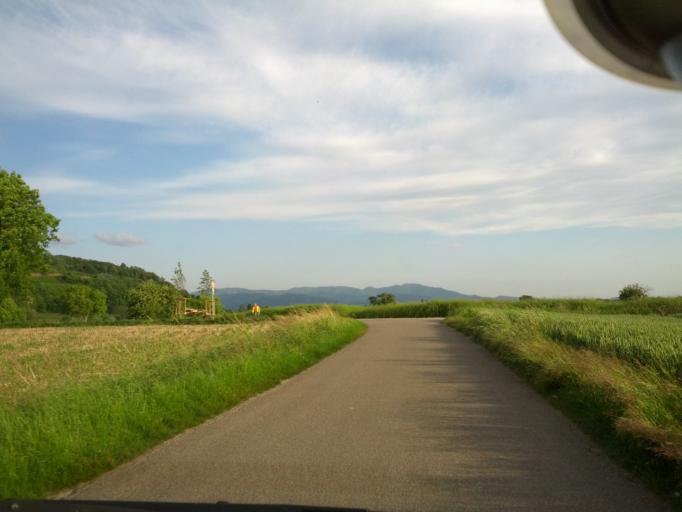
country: DE
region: Baden-Wuerttemberg
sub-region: Freiburg Region
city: Merdingen
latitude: 47.9810
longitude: 7.6709
